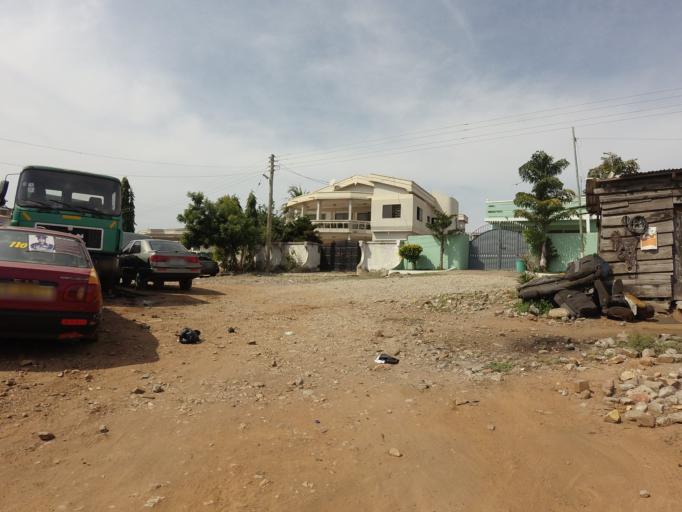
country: GH
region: Greater Accra
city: Dome
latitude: 5.6254
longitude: -0.2317
